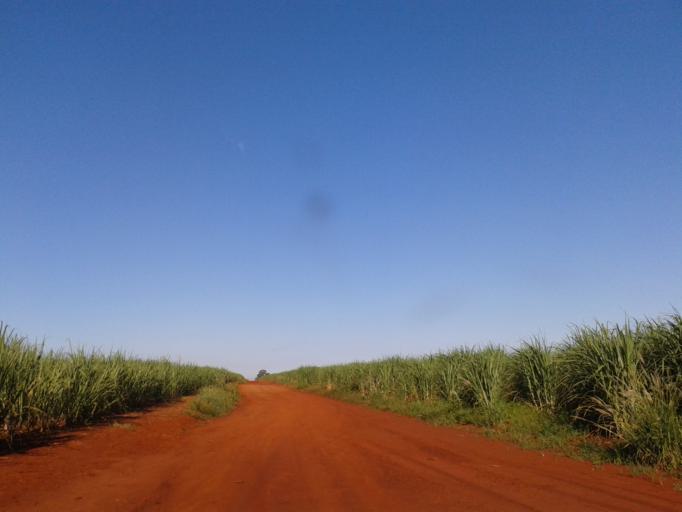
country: BR
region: Minas Gerais
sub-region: Centralina
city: Centralina
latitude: -18.6717
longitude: -49.2783
